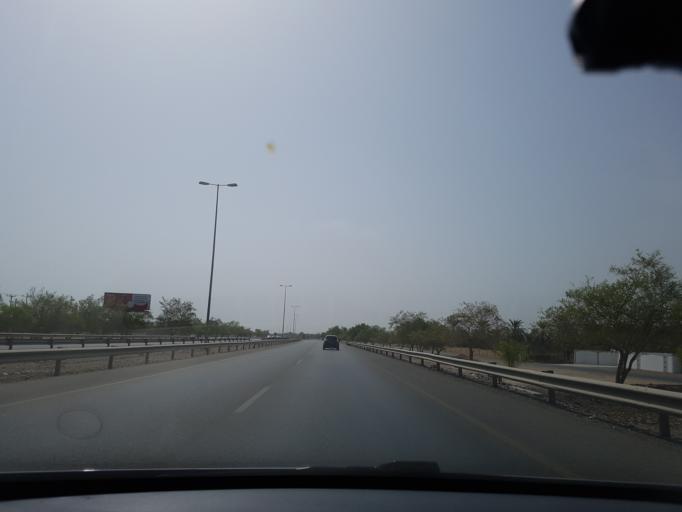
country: OM
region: Al Batinah
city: Al Khaburah
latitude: 23.9460
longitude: 57.1141
